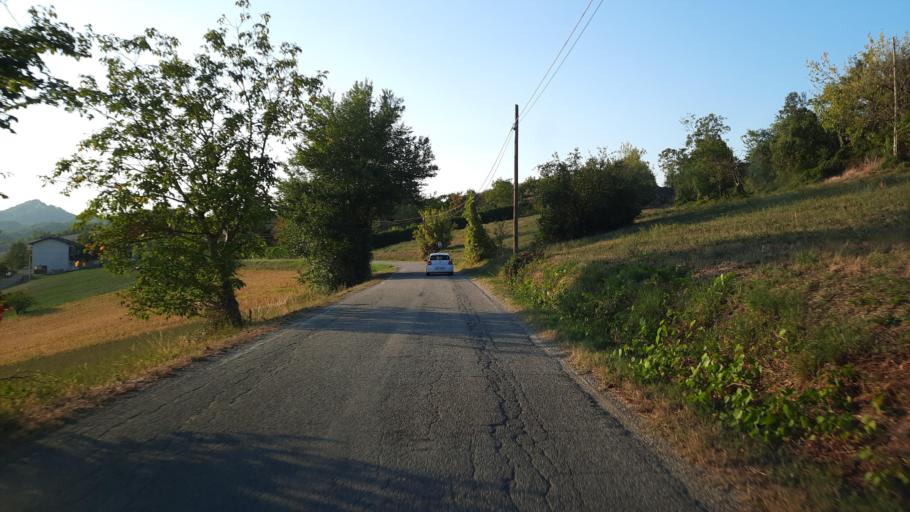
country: IT
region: Piedmont
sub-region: Provincia di Alessandria
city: Cereseto
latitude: 45.0747
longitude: 8.3279
